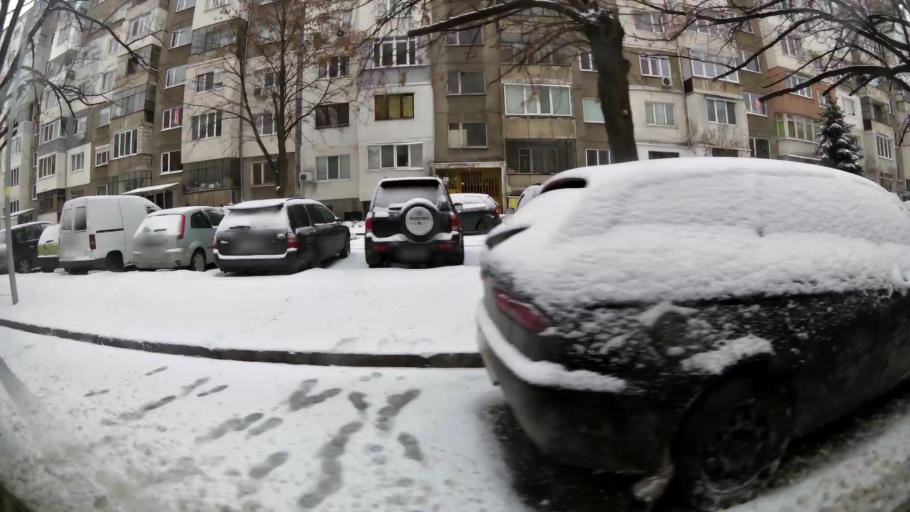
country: BG
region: Sofia-Capital
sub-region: Stolichna Obshtina
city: Sofia
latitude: 42.6950
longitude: 23.2996
